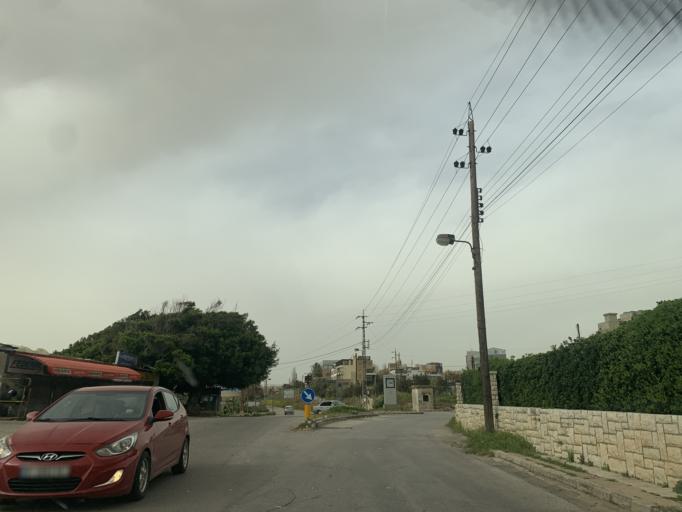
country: LB
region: Mont-Liban
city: Jbail
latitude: 34.1043
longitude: 35.6518
